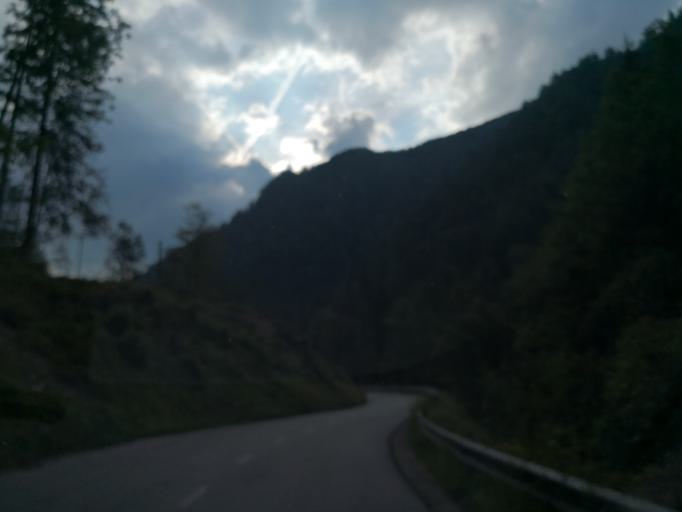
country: SI
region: Jezersko
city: Zgornje Jezersko
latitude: 46.3854
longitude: 14.4732
